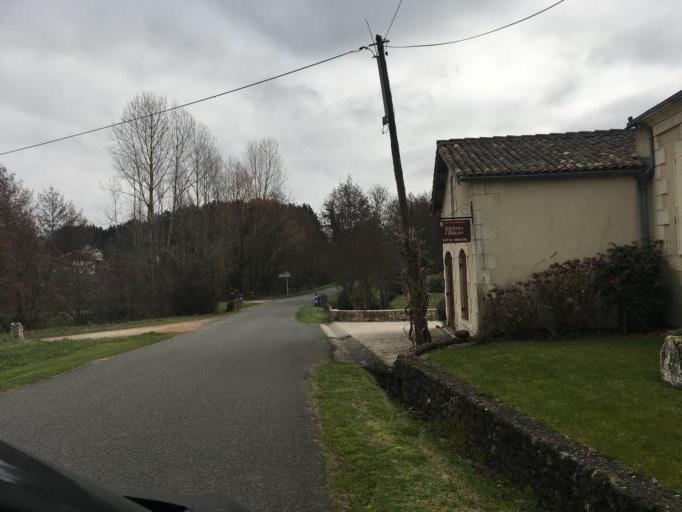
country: FR
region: Poitou-Charentes
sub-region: Departement de la Charente-Maritime
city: Mirambeau
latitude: 45.3265
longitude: -0.5728
